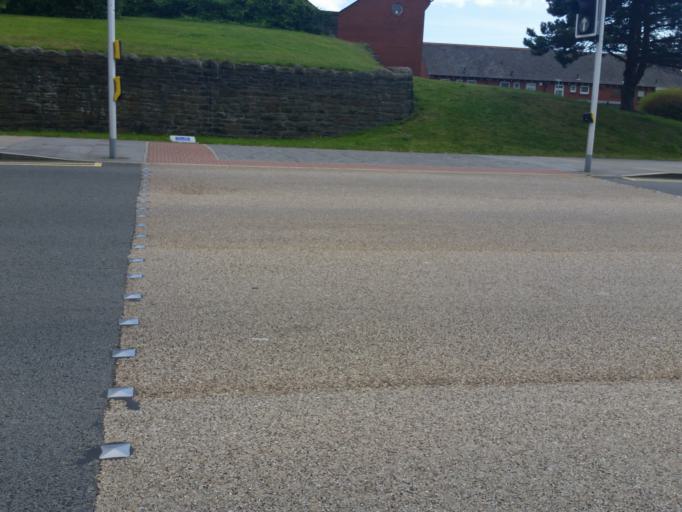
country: GB
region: Wales
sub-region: City and County of Swansea
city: Swansea
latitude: 51.6156
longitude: -3.9452
